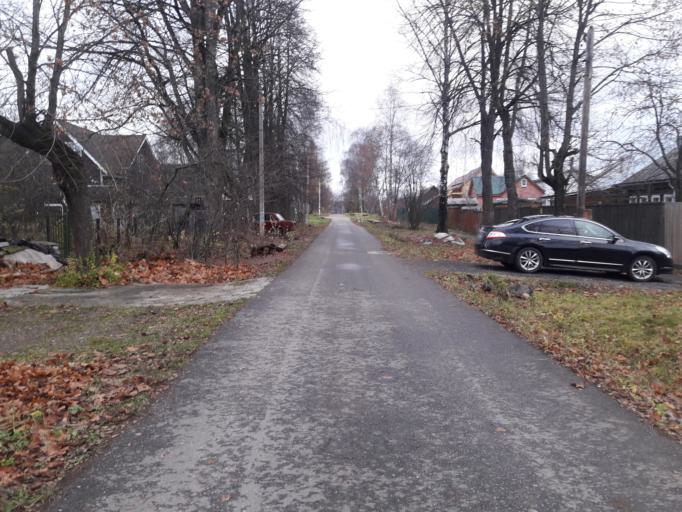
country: RU
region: Moskovskaya
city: Ashukino
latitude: 56.1650
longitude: 37.9378
